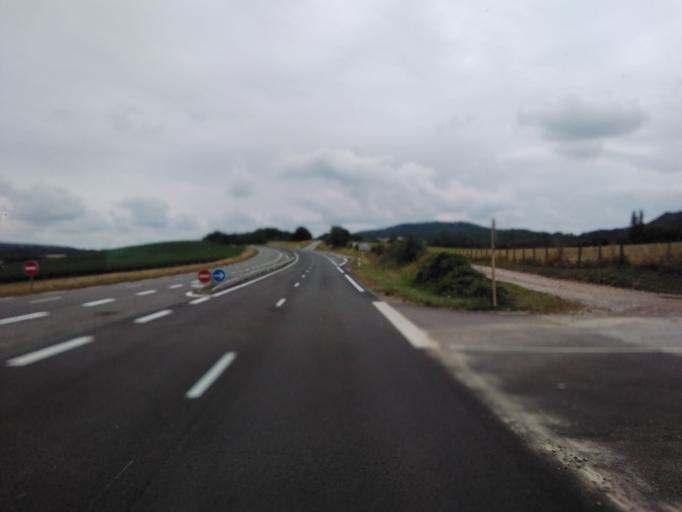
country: FR
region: Franche-Comte
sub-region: Departement du Jura
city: Montmorot
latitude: 46.7432
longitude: 5.5555
